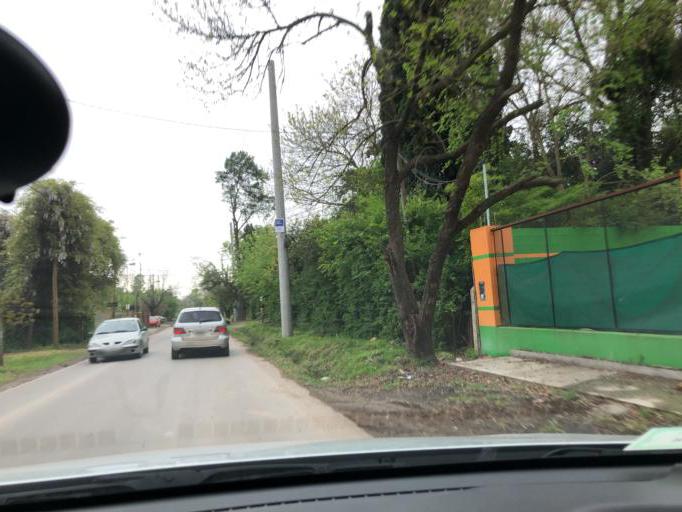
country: AR
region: Buenos Aires
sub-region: Partido de La Plata
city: La Plata
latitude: -34.8919
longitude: -58.0643
